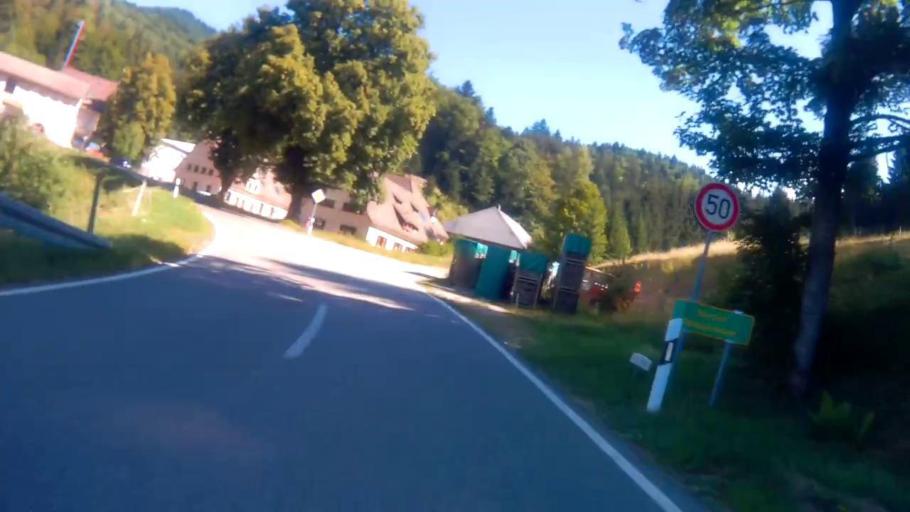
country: DE
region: Baden-Wuerttemberg
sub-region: Freiburg Region
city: Sulzburg
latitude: 47.7816
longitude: 7.7361
